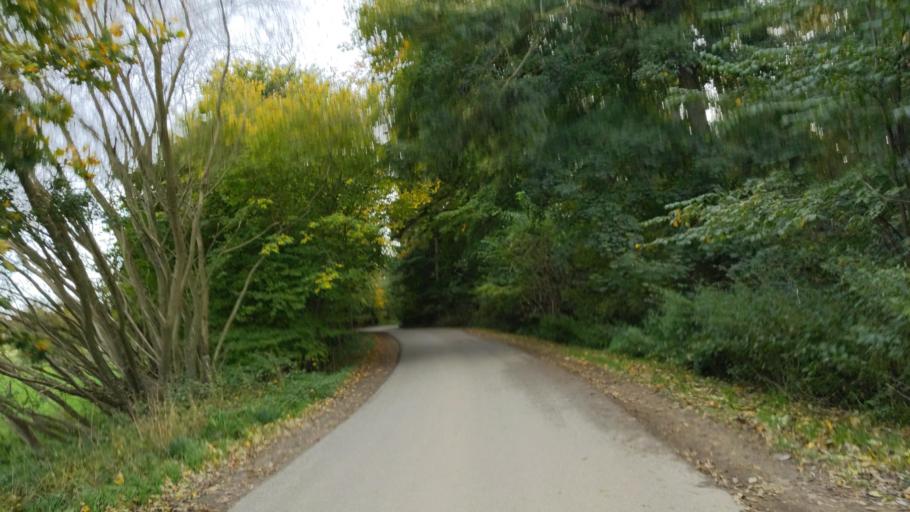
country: DE
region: Schleswig-Holstein
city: Susel
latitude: 54.1128
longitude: 10.7060
